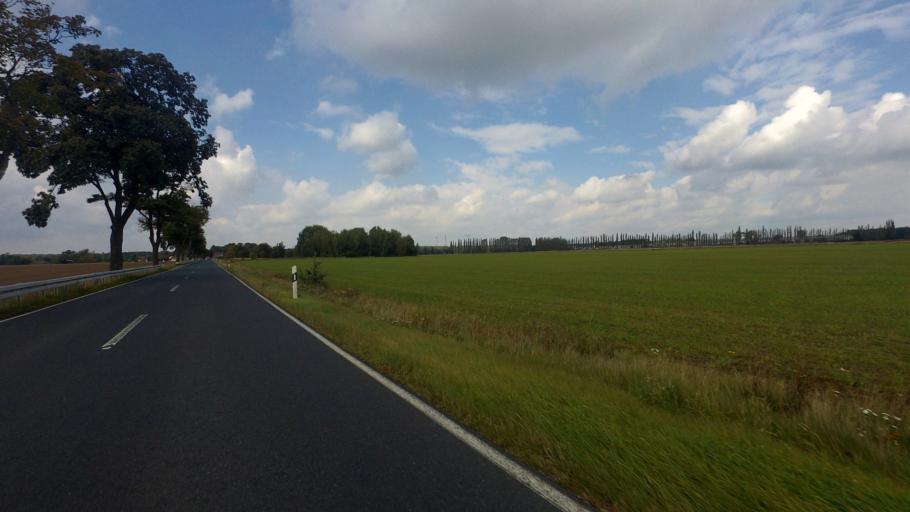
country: DE
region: Saxony-Anhalt
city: Holzdorf
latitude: 51.8321
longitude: 13.1543
